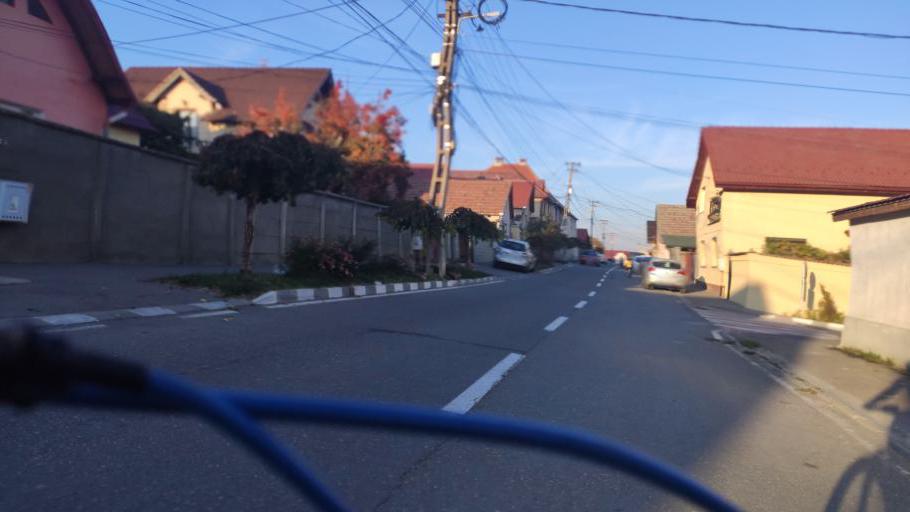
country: RO
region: Brasov
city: Codlea
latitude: 45.6928
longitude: 25.4404
